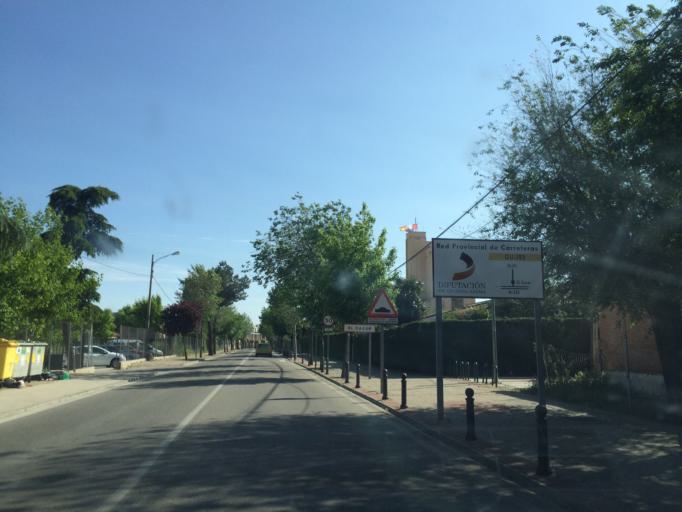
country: ES
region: Madrid
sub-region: Provincia de Madrid
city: Ribatejada
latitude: 40.7057
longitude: -3.4275
